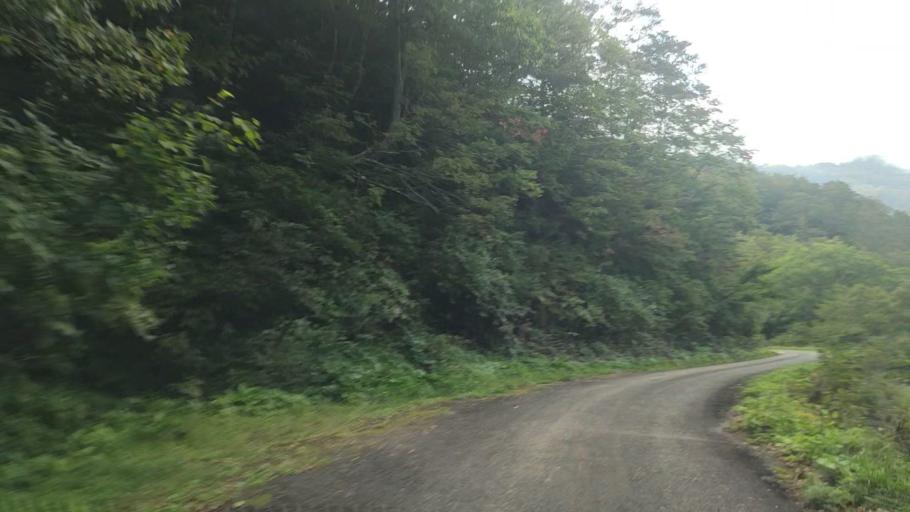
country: JP
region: Toyama
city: Yatsuomachi-higashikumisaka
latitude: 36.3505
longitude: 137.0645
